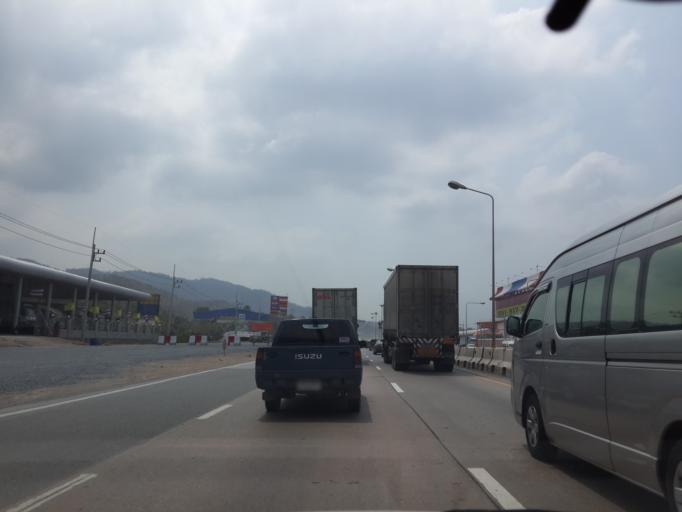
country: TH
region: Chon Buri
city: Chon Buri
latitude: 13.3090
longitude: 100.9933
